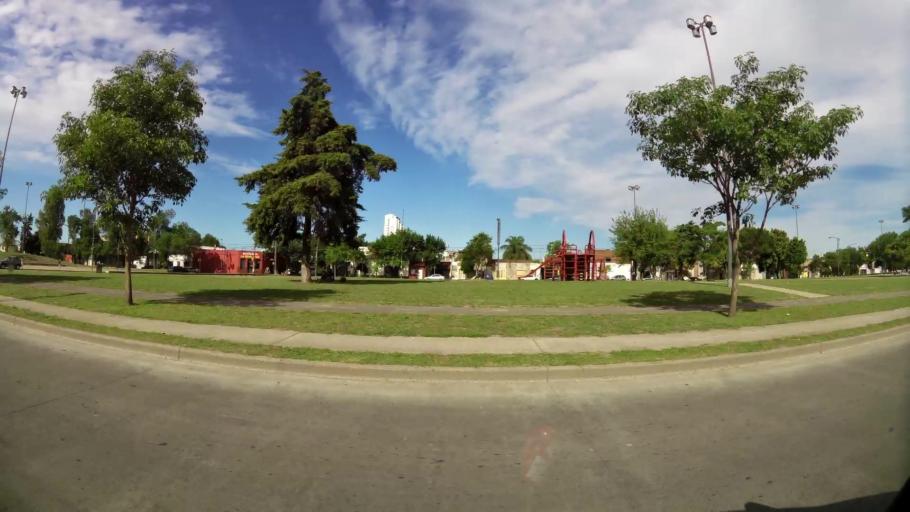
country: AR
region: Santa Fe
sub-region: Departamento de Rosario
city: Rosario
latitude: -32.9160
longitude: -60.6916
